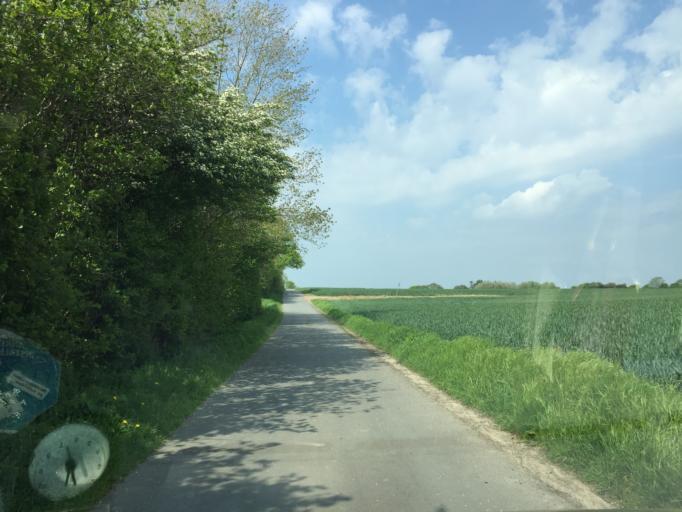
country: DK
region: South Denmark
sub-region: Langeland Kommune
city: Rudkobing
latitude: 54.9884
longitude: 10.8152
